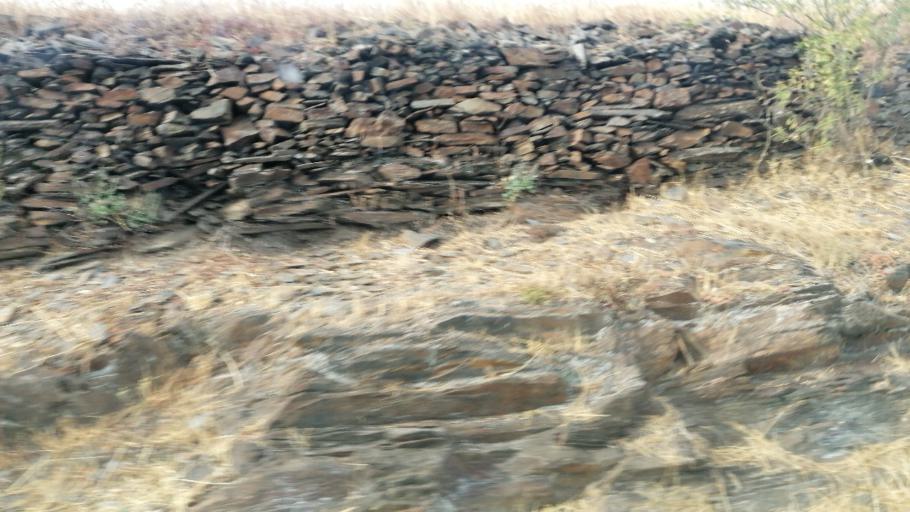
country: PT
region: Viseu
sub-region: Penedono
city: Penedono
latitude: 41.0670
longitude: -7.4000
